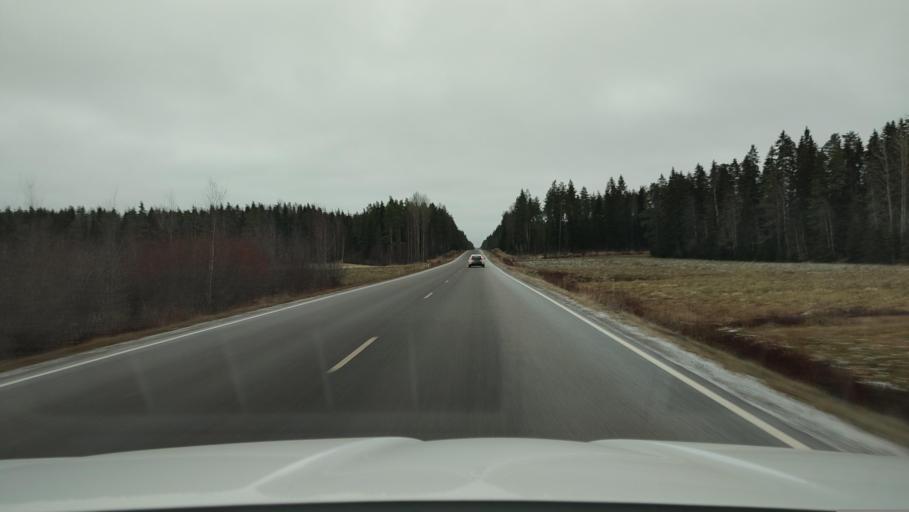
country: FI
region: Ostrobothnia
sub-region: Sydosterbotten
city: Naerpes
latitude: 62.5833
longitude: 21.4956
